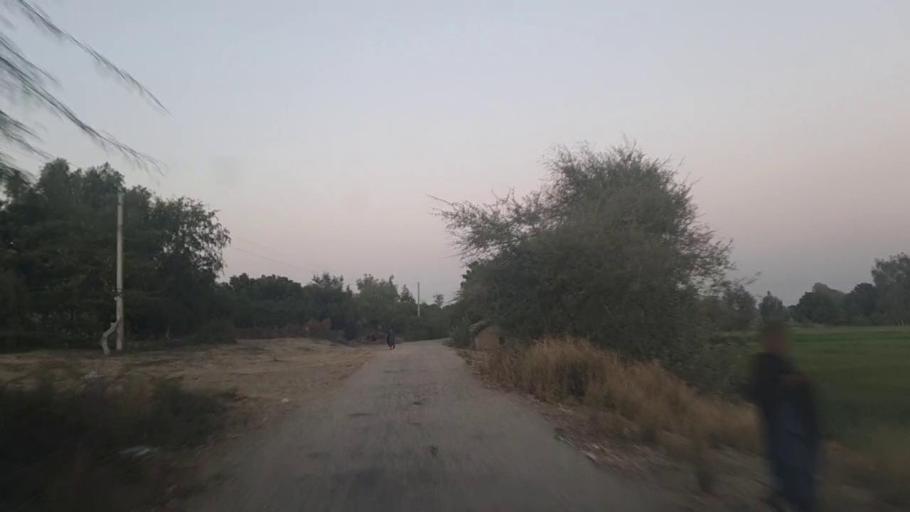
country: PK
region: Sindh
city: Jam Sahib
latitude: 26.3881
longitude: 68.8182
